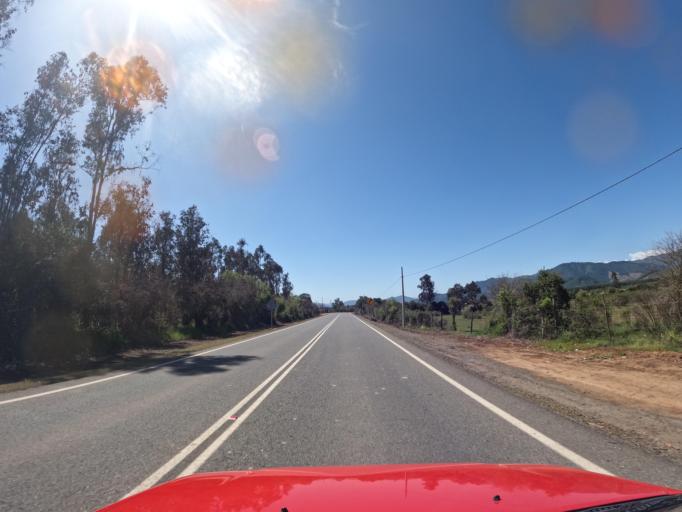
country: CL
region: Maule
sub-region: Provincia de Talca
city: San Clemente
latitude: -35.4437
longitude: -71.2664
